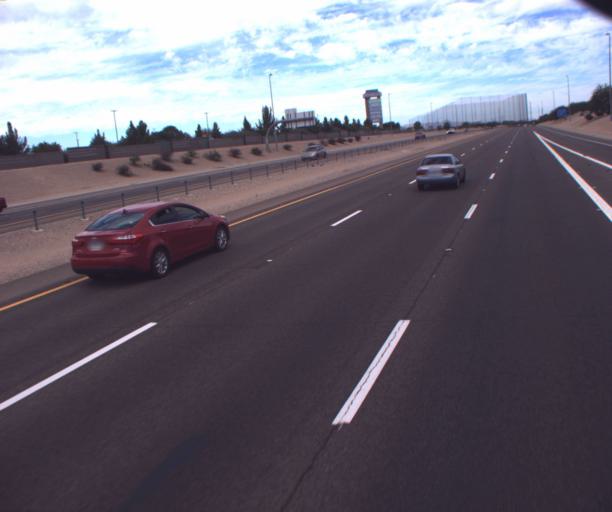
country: US
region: Arizona
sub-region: Maricopa County
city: Gilbert
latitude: 33.3108
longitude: -111.7392
